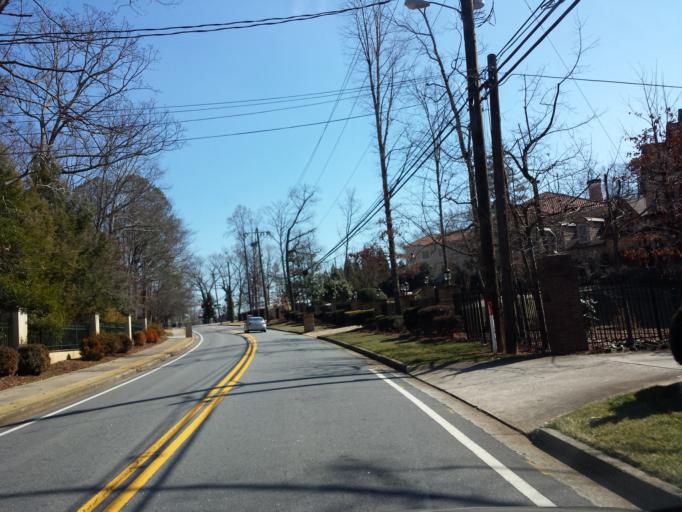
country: US
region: Georgia
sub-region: Fulton County
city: Sandy Springs
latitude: 33.9173
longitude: -84.3990
